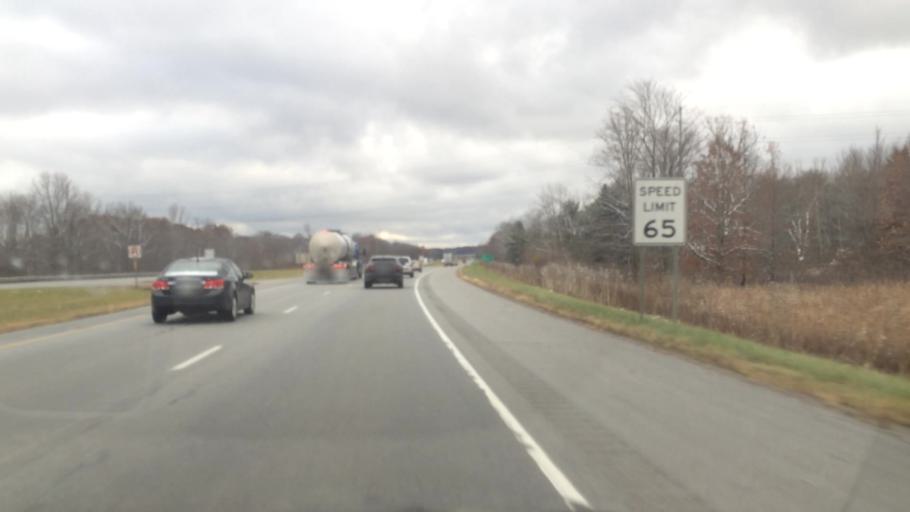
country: US
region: Ohio
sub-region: Summit County
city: Twinsburg
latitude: 41.2999
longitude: -81.4295
